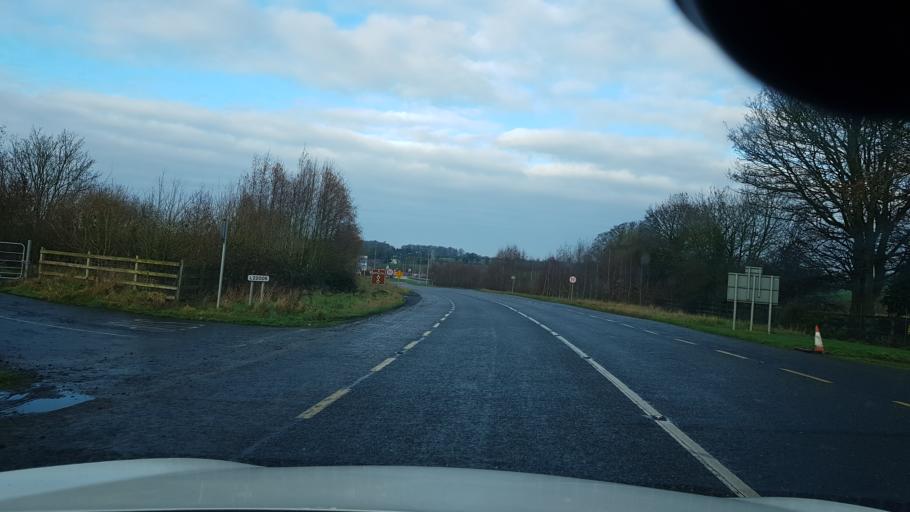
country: IE
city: Kentstown
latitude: 53.5969
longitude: -6.6089
